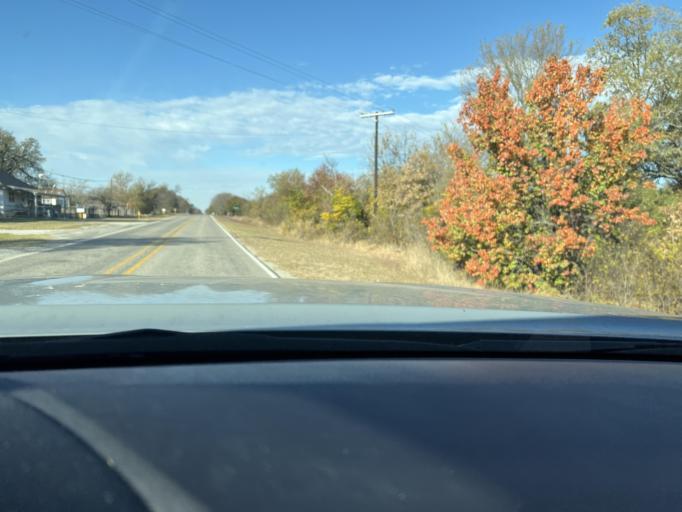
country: US
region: Texas
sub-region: Eastland County
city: Ranger
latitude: 32.4193
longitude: -98.7400
